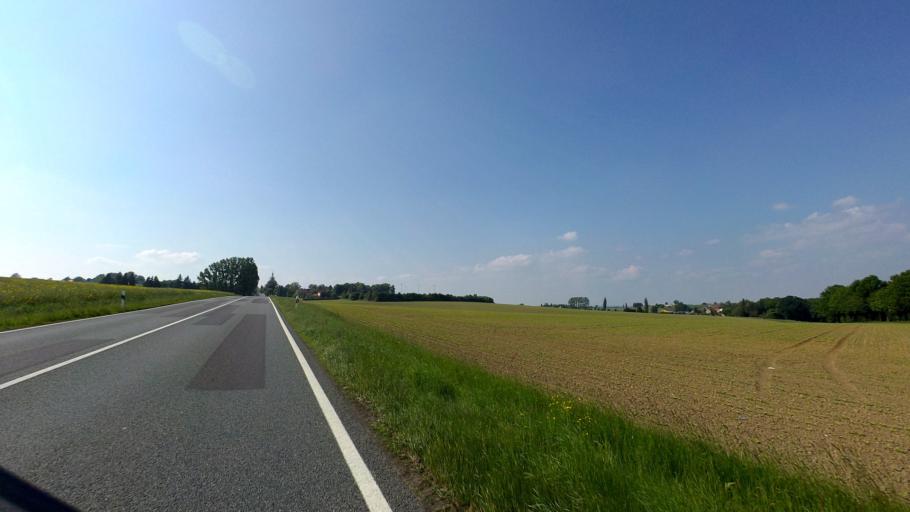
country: DE
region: Saxony
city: Hochkirch
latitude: 51.1438
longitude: 14.5825
